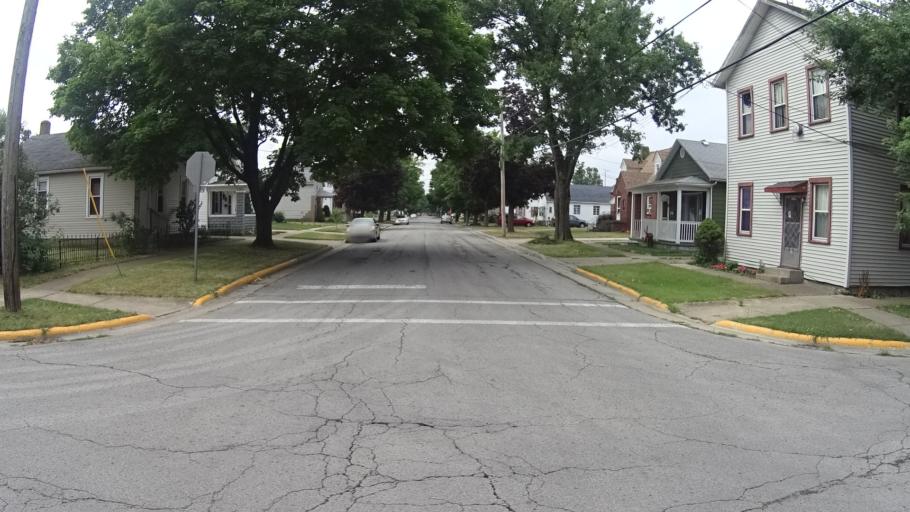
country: US
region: Ohio
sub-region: Erie County
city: Sandusky
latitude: 41.4492
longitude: -82.7219
